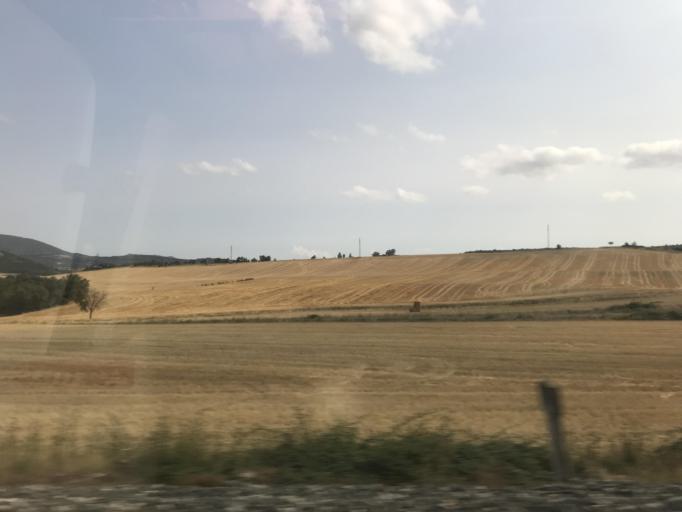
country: ES
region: Basque Country
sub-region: Provincia de Alava
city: Arminon
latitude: 42.7021
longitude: -2.8939
